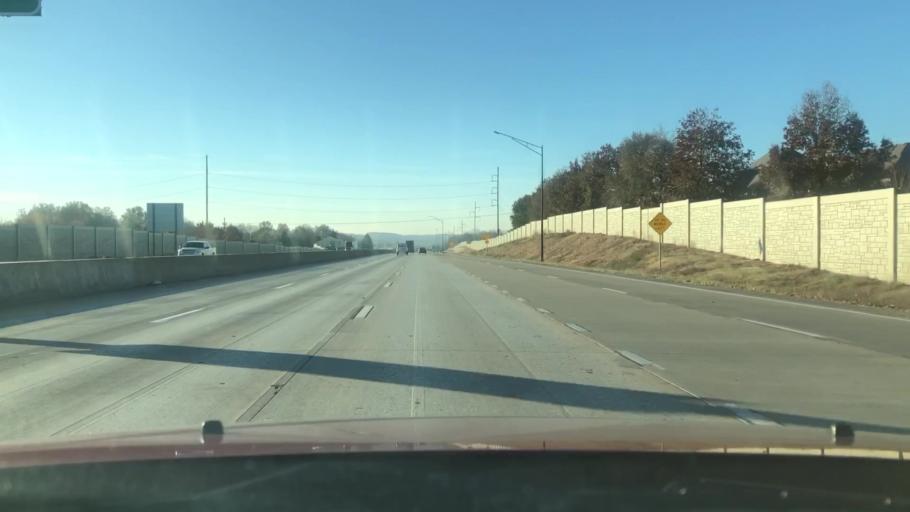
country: US
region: Missouri
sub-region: Greene County
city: Springfield
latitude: 37.1529
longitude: -93.2247
